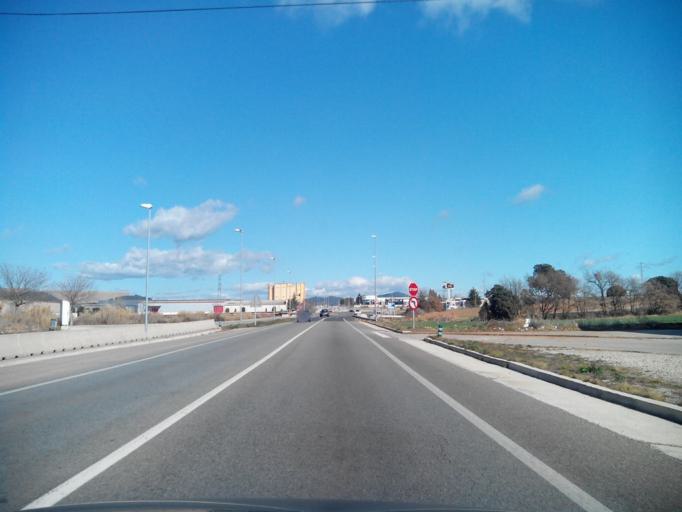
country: ES
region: Catalonia
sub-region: Provincia de Barcelona
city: Sant Fruitos de Bages
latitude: 41.7615
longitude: 1.8715
